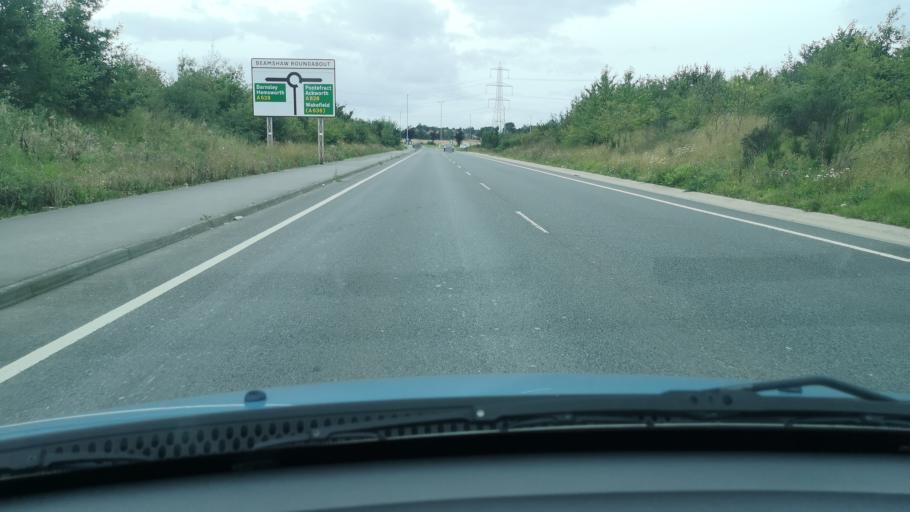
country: GB
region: England
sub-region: City and Borough of Wakefield
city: Hemsworth
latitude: 53.6053
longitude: -1.3360
